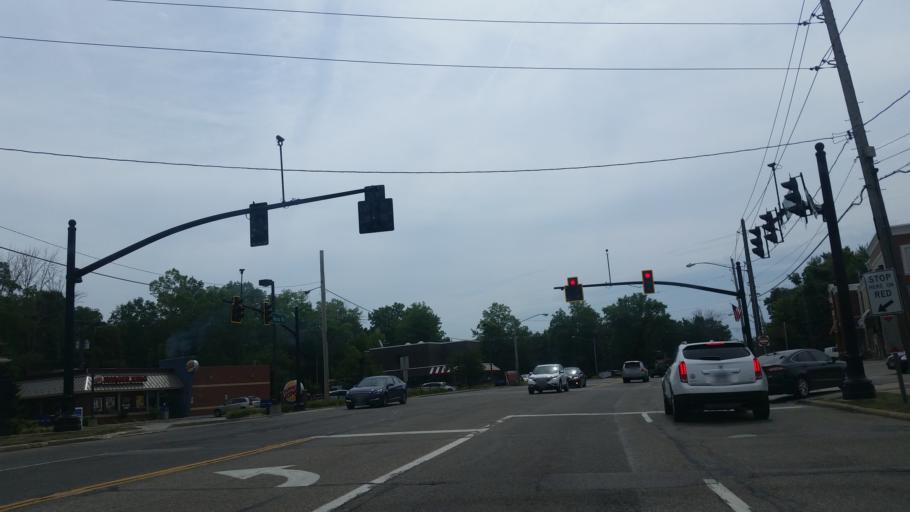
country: US
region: Ohio
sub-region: Cuyahoga County
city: Solon
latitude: 41.3847
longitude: -81.4355
